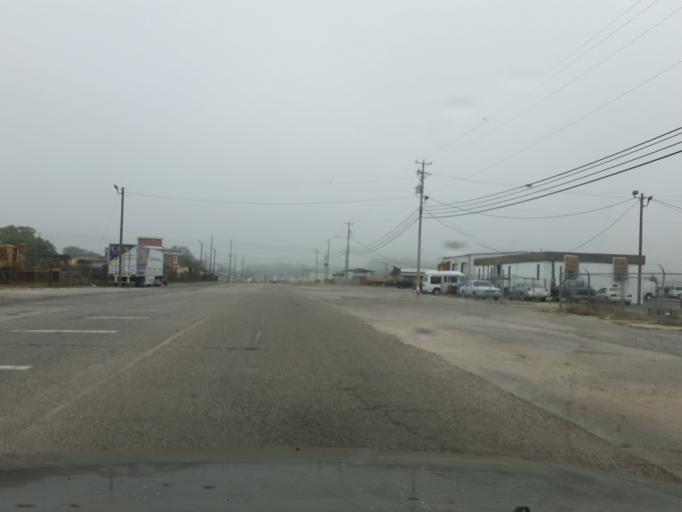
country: US
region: Florida
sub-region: Escambia County
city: Ferry Pass
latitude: 30.5250
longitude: -87.1977
